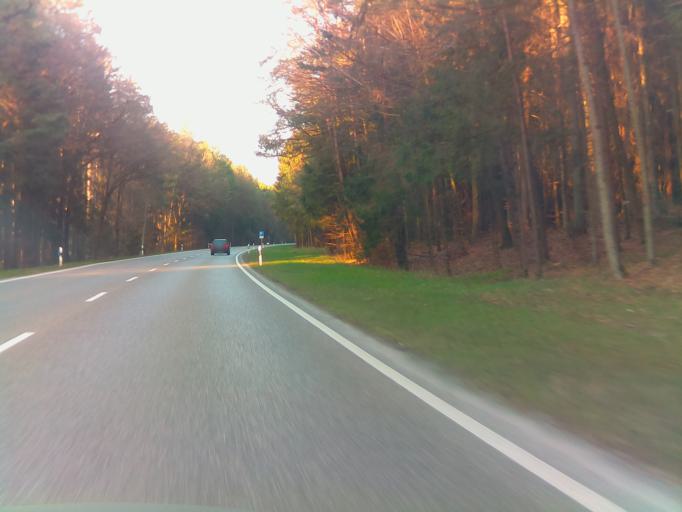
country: DE
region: Bavaria
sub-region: Upper Bavaria
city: Munchsmunster
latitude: 48.7473
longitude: 11.6543
